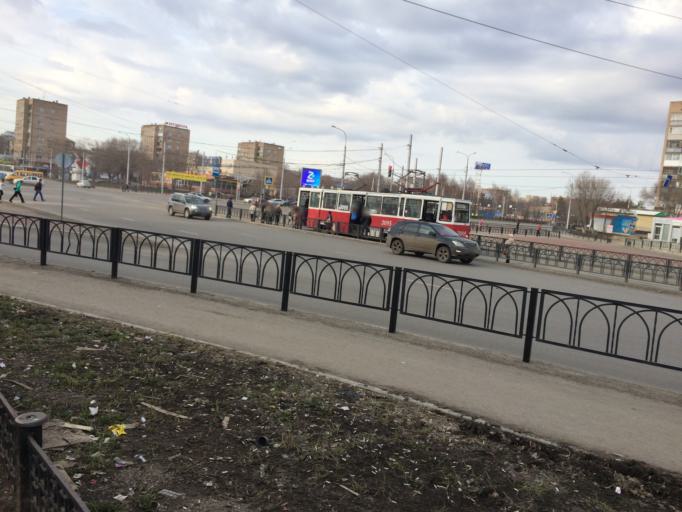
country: RU
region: Chelyabinsk
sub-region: Gorod Magnitogorsk
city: Magnitogorsk
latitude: 53.3988
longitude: 58.9786
